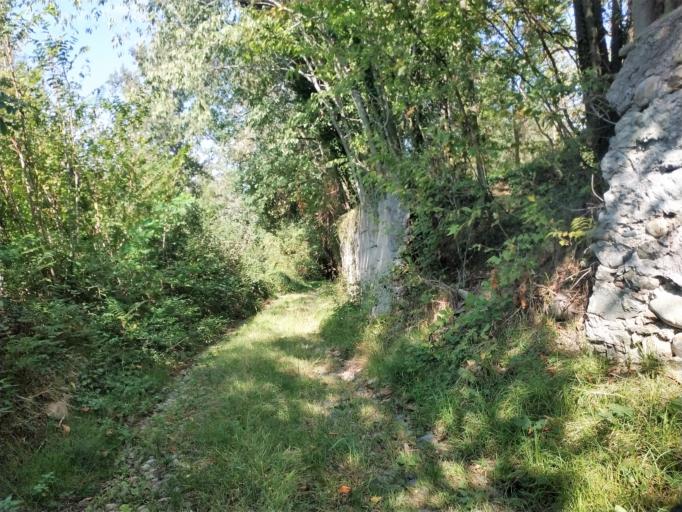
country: IT
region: Piedmont
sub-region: Provincia di Torino
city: Orio Canavese
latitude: 45.3298
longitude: 7.8554
